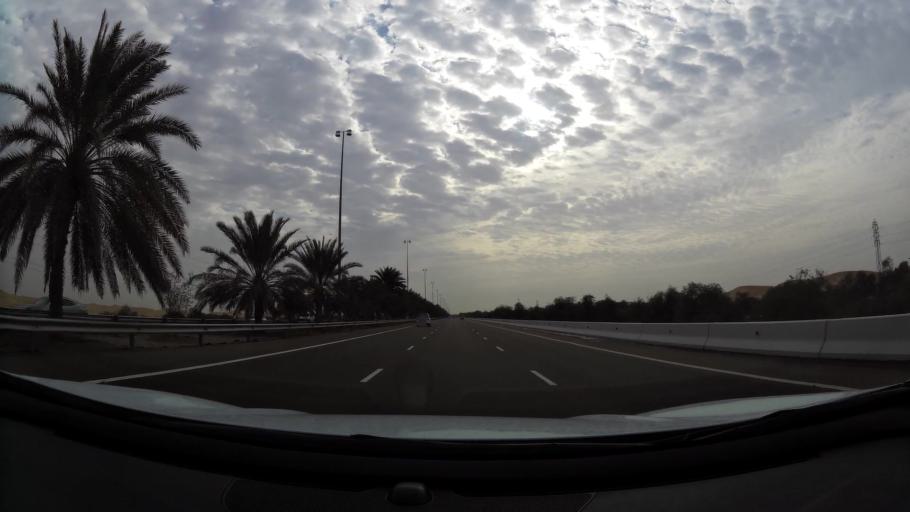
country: AE
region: Abu Dhabi
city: Al Ain
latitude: 24.1736
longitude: 55.2082
